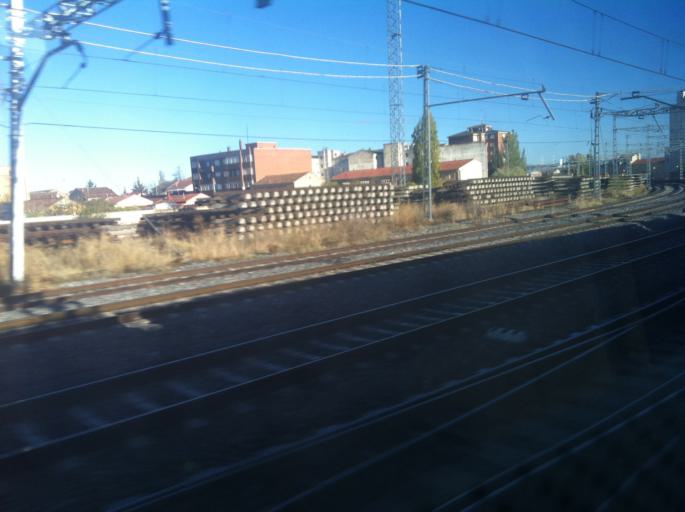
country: ES
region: Castille and Leon
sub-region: Provincia de Palencia
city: Venta de Banos
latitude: 41.9205
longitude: -4.4927
